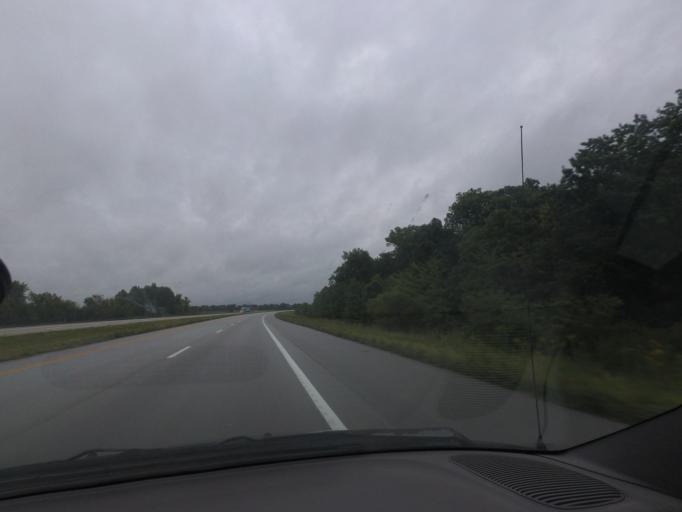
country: US
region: Missouri
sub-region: Marion County
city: Monroe City
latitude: 39.6624
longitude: -91.7434
